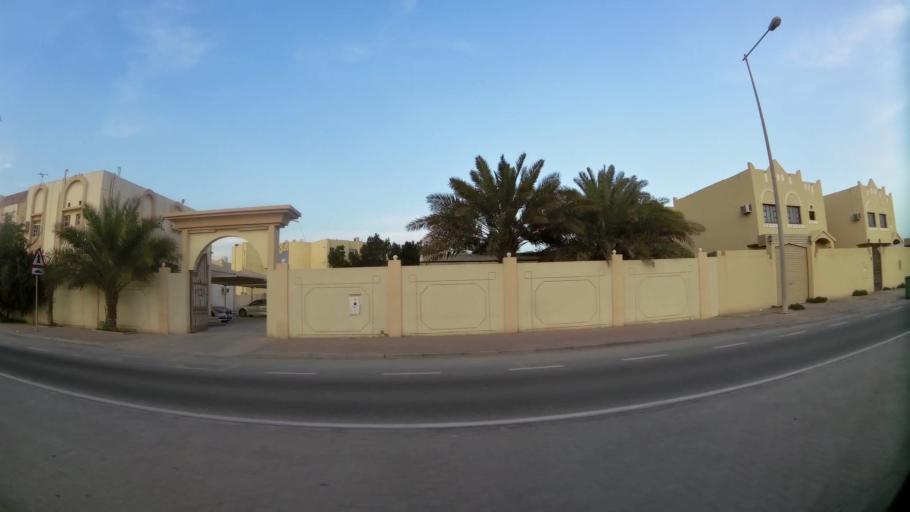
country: QA
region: Al Wakrah
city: Al Wakrah
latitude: 25.1873
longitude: 51.6076
